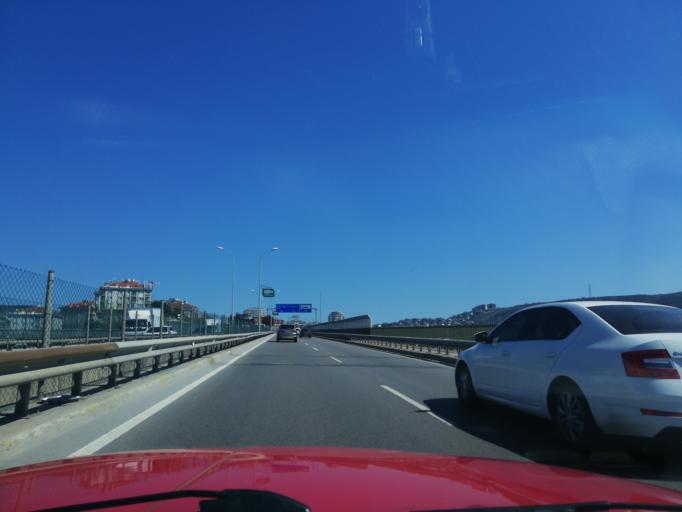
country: TR
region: Istanbul
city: Umraniye
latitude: 41.1057
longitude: 29.1042
